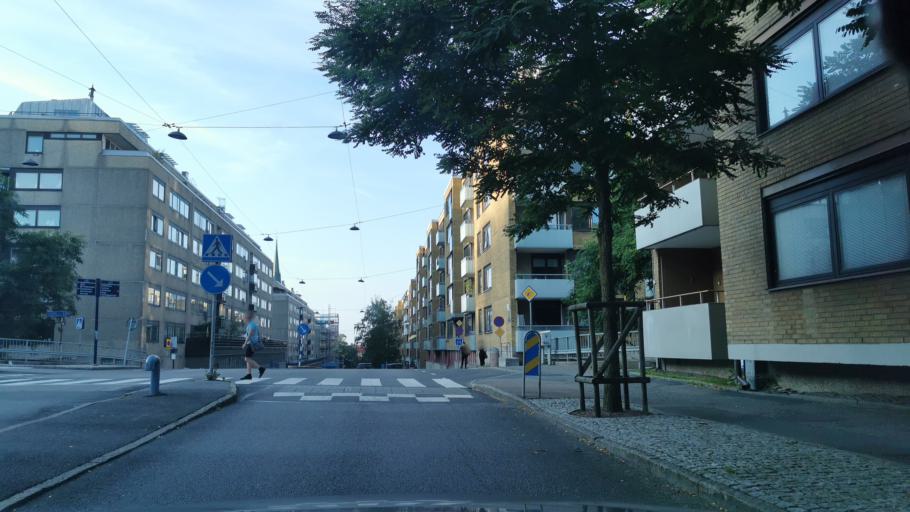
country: SE
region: Vaestra Goetaland
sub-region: Goteborg
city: Goeteborg
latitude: 57.6935
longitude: 11.9481
